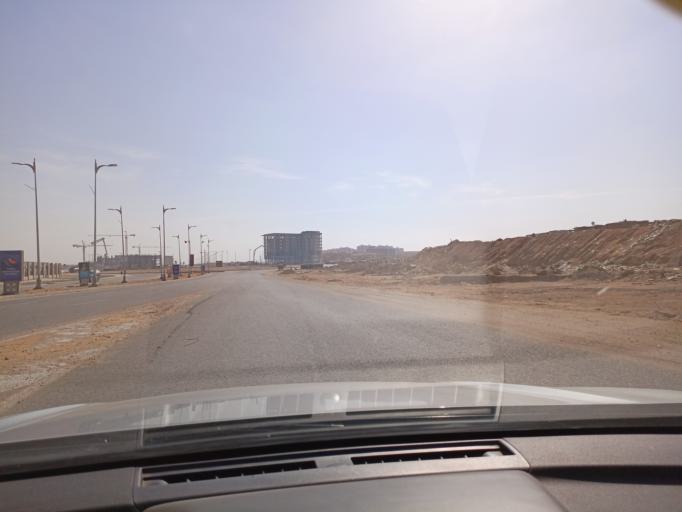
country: EG
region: Muhafazat al Qalyubiyah
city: Al Khankah
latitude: 30.0407
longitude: 31.6852
